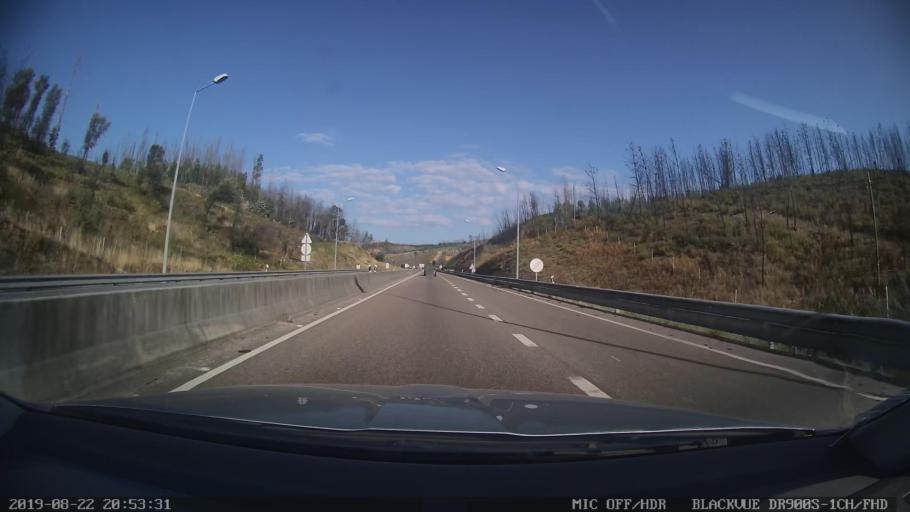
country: PT
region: Castelo Branco
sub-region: Proenca-A-Nova
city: Proenca-a-Nova
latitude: 39.7710
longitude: -7.9938
